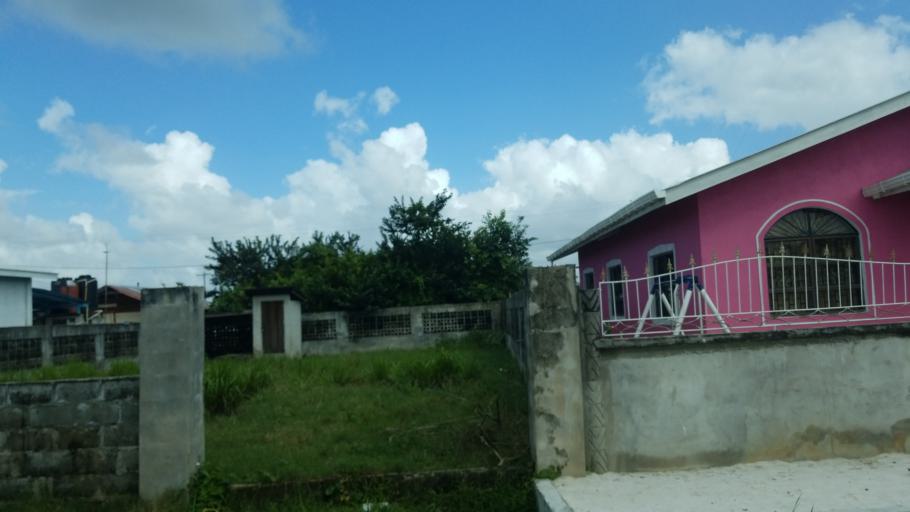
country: GY
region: Essequibo Islands-West Demerara
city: Vreed-en-Hoop
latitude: 6.7812
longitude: -58.2259
